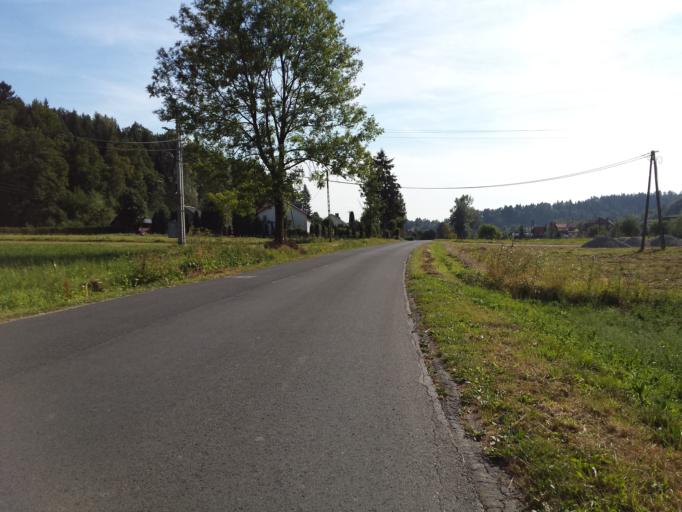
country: PL
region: Subcarpathian Voivodeship
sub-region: Powiat leski
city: Olszanica
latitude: 49.4913
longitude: 22.4483
